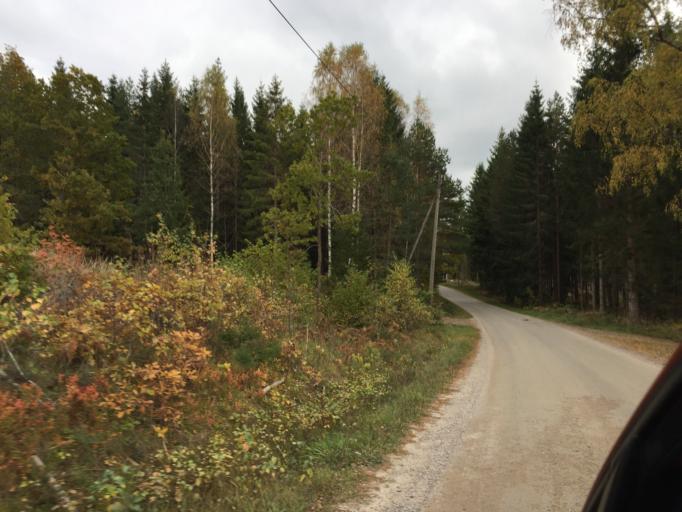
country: SE
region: Soedermanland
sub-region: Vingakers Kommun
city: Vingaker
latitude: 59.0109
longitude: 15.7814
